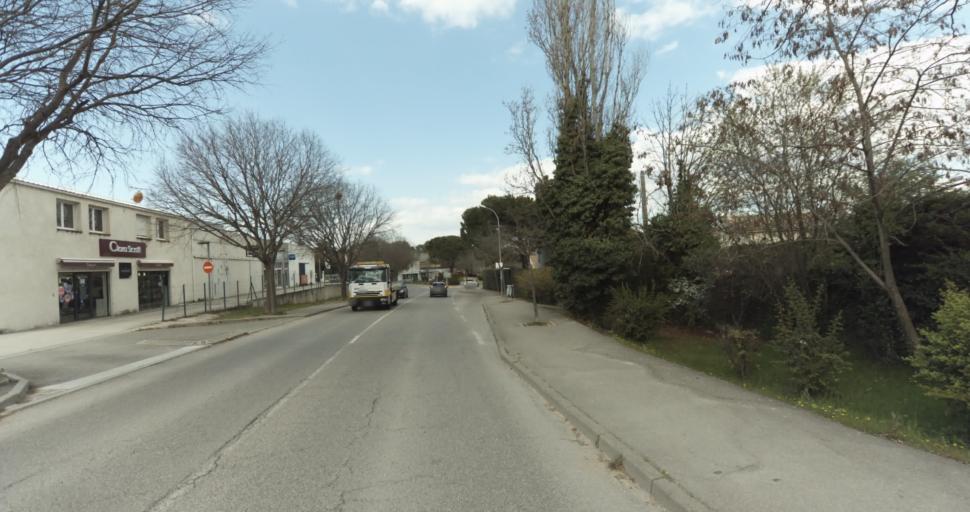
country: FR
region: Provence-Alpes-Cote d'Azur
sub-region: Departement des Bouches-du-Rhone
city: Greasque
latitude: 43.4341
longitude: 5.5413
